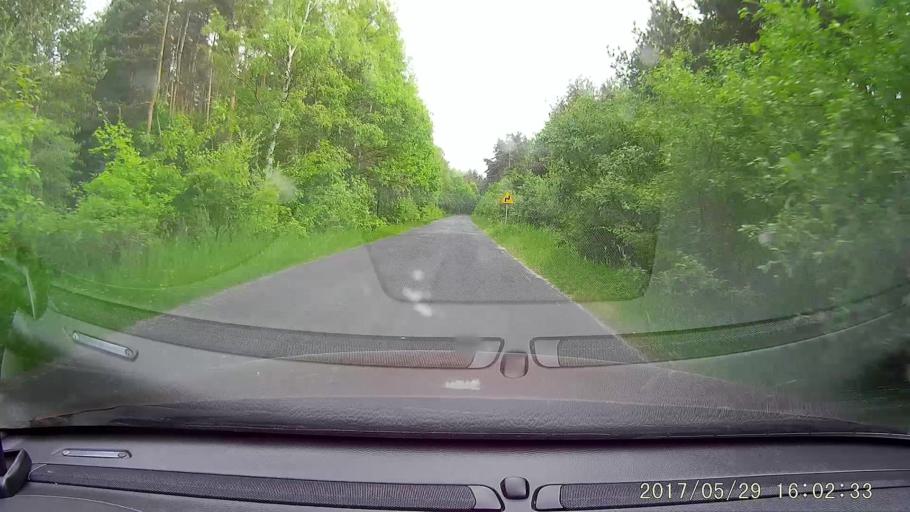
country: PL
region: Lower Silesian Voivodeship
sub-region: Powiat zgorzelecki
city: Wegliniec
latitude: 51.2275
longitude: 15.2078
